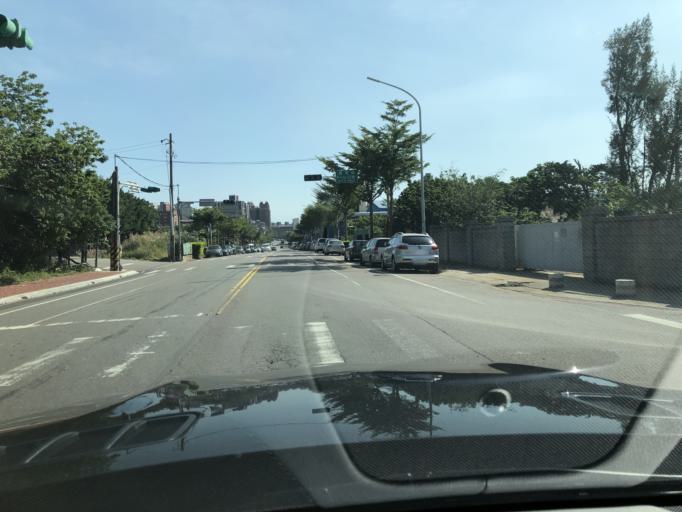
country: TW
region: Taiwan
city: Taoyuan City
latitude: 25.0659
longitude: 121.2909
